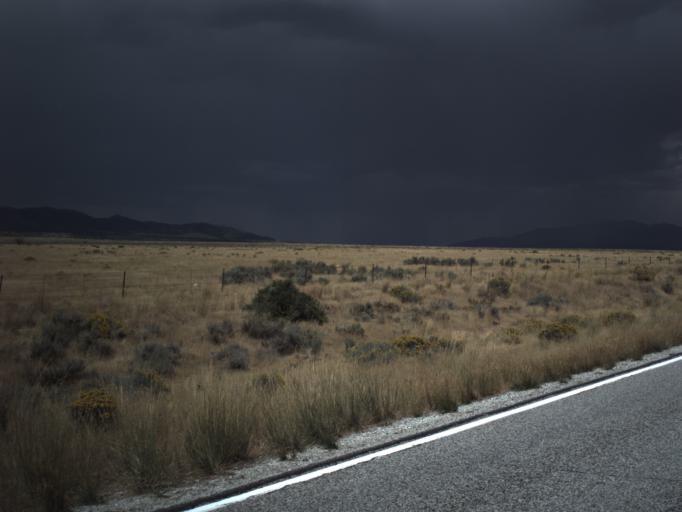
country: US
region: Idaho
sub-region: Minidoka County
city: Rupert
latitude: 41.8547
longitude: -113.1320
